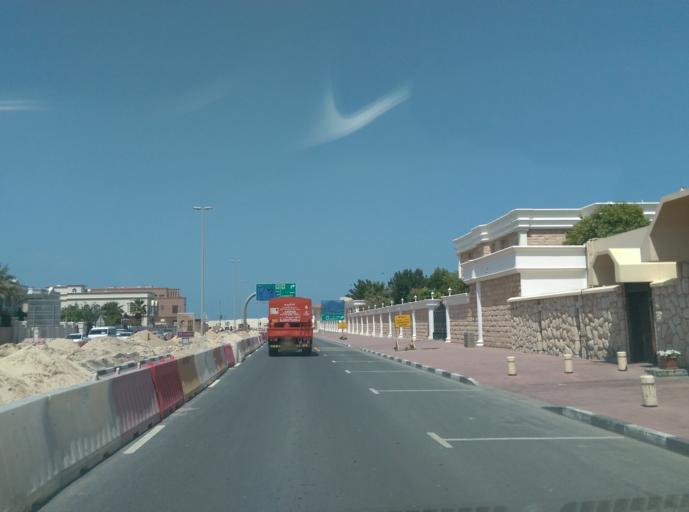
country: AE
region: Dubai
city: Dubai
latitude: 25.1918
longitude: 55.2364
